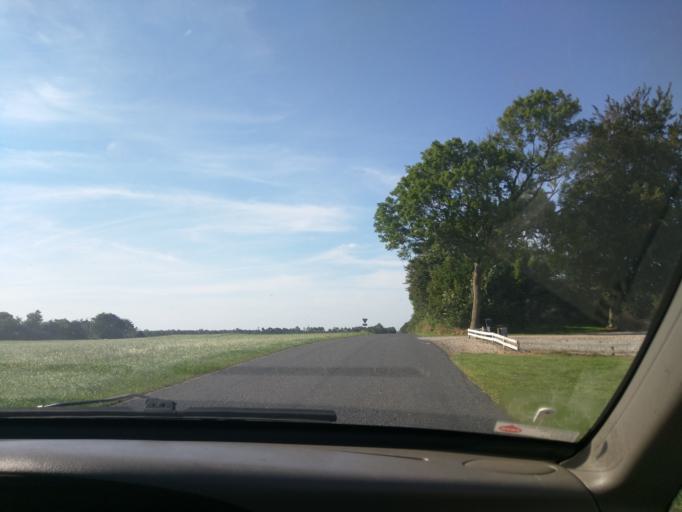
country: DK
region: Central Jutland
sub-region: Viborg Kommune
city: Bjerringbro
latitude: 56.4805
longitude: 9.6047
